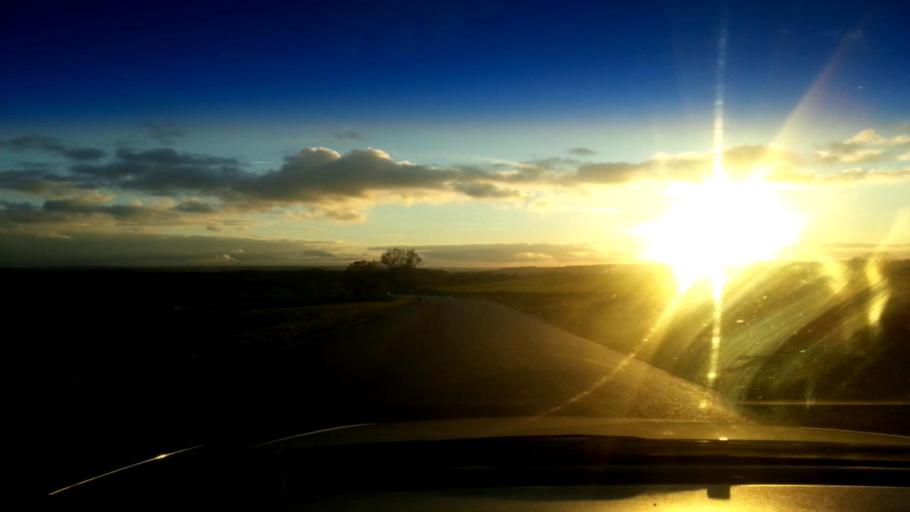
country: DE
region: Bavaria
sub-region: Upper Franconia
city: Buttenheim
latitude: 49.8130
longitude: 11.0515
